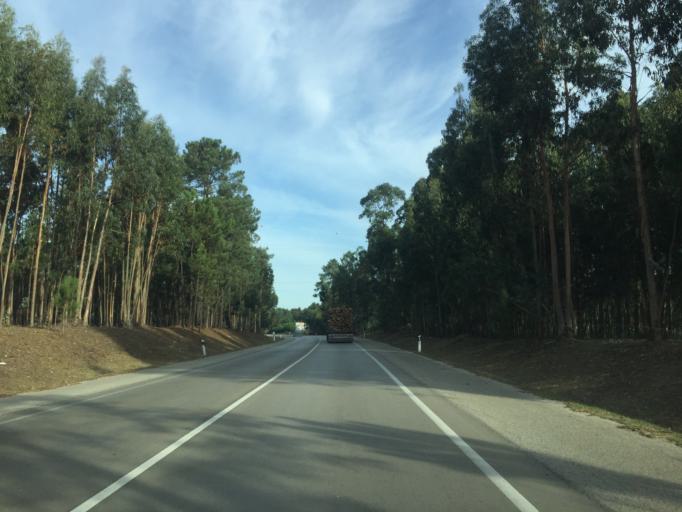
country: PT
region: Leiria
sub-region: Pombal
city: Lourical
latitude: 40.0113
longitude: -8.8070
